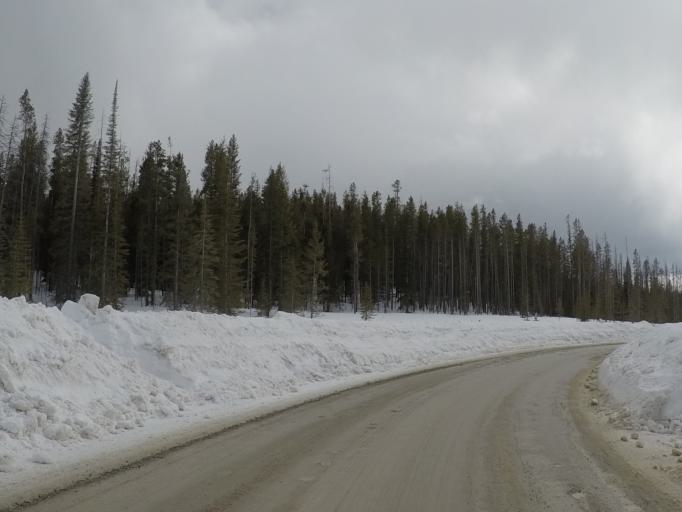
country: US
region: Montana
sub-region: Granite County
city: Philipsburg
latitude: 46.2320
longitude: -113.2460
